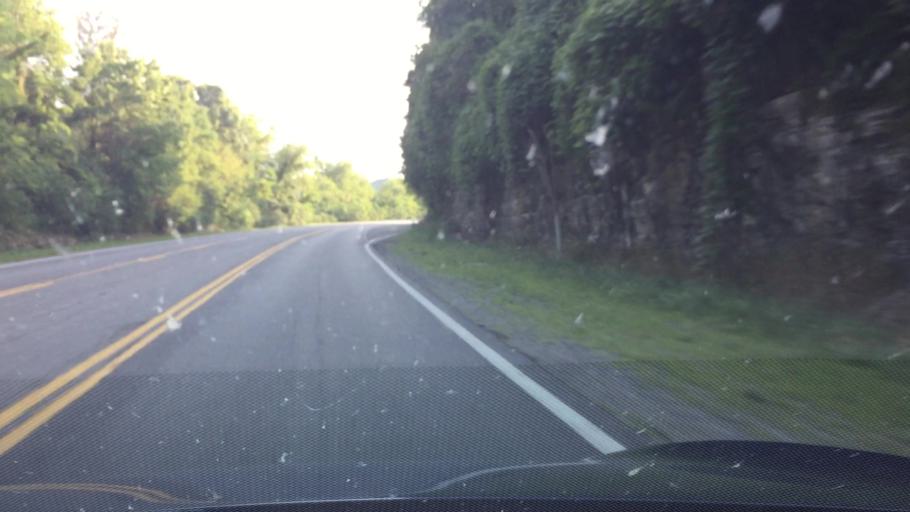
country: US
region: Virginia
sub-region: Pulaski County
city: Dublin
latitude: 37.1239
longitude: -80.6519
